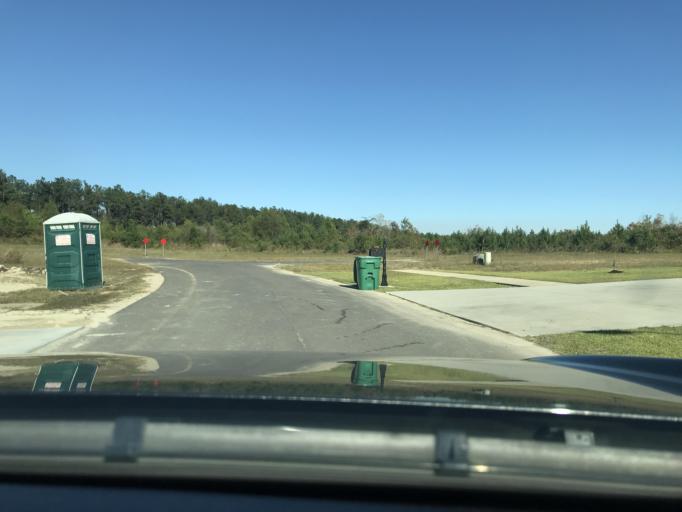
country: US
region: Louisiana
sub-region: Calcasieu Parish
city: Moss Bluff
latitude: 30.3129
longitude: -93.2561
